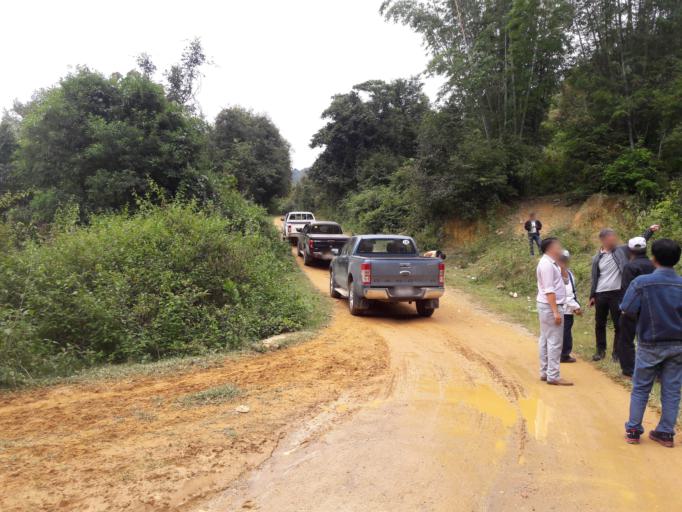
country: LA
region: Houaphan
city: Xam Nua
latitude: 20.3267
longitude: 104.0018
